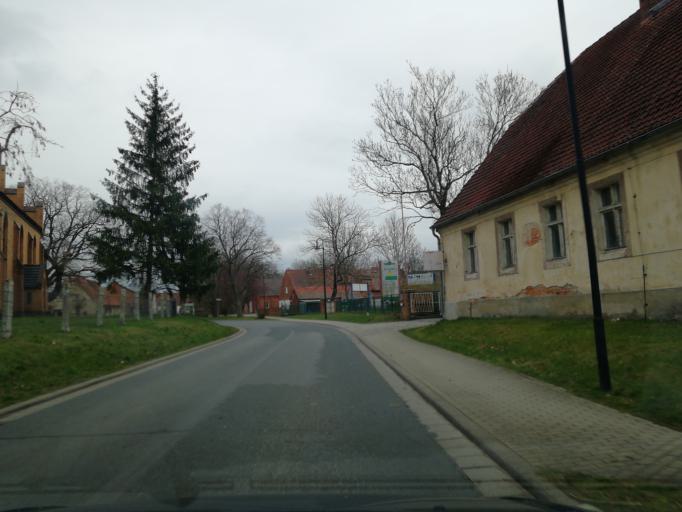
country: DE
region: Brandenburg
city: Vetschau
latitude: 51.7274
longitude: 14.0509
